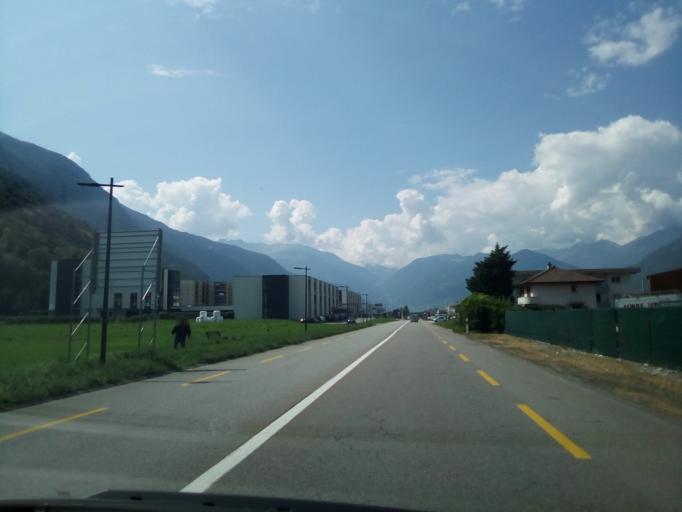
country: CH
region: Valais
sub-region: Martigny District
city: Saxon
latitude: 46.1455
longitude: 7.1664
